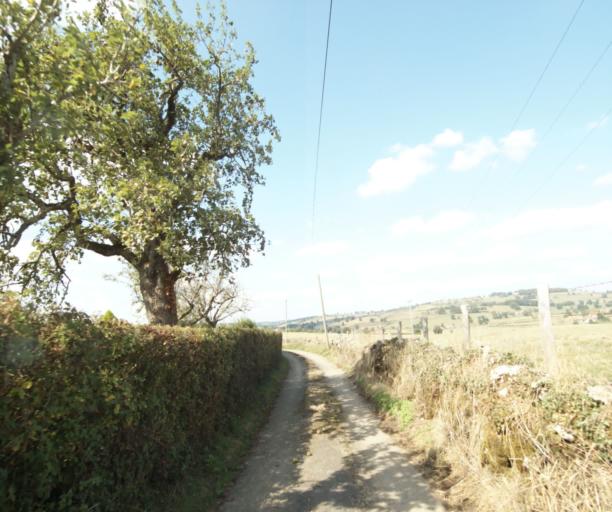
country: FR
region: Bourgogne
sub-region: Departement de Saone-et-Loire
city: Charolles
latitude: 46.3581
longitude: 4.2409
